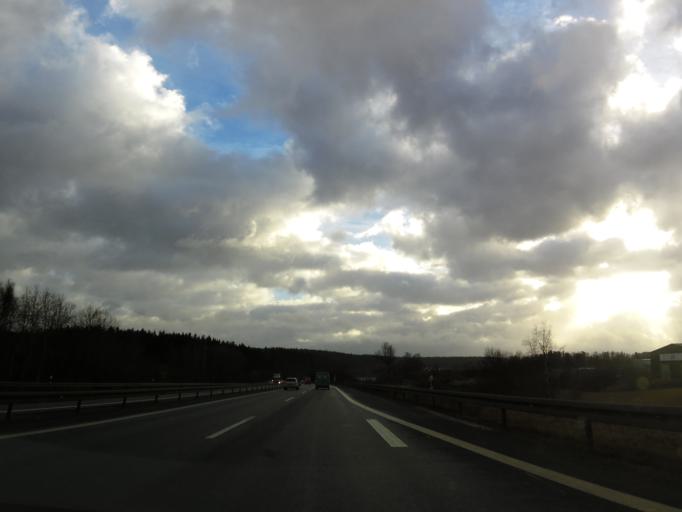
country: DE
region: Bavaria
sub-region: Upper Franconia
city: Selb
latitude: 50.1666
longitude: 12.1071
